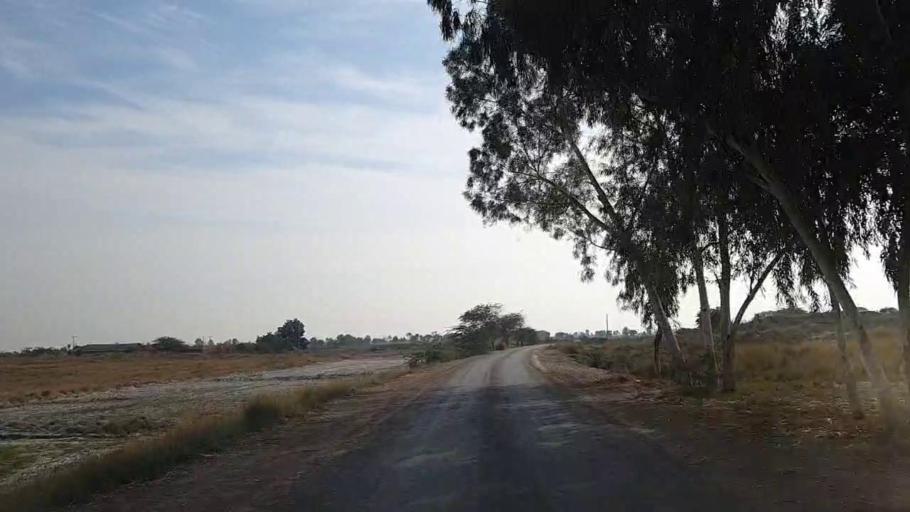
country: PK
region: Sindh
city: Daur
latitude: 26.4706
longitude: 68.4181
